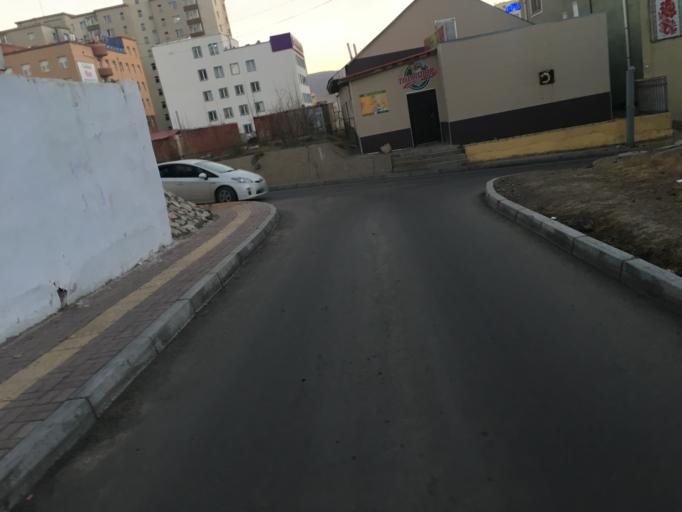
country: MN
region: Ulaanbaatar
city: Ulaanbaatar
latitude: 47.9254
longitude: 106.8886
